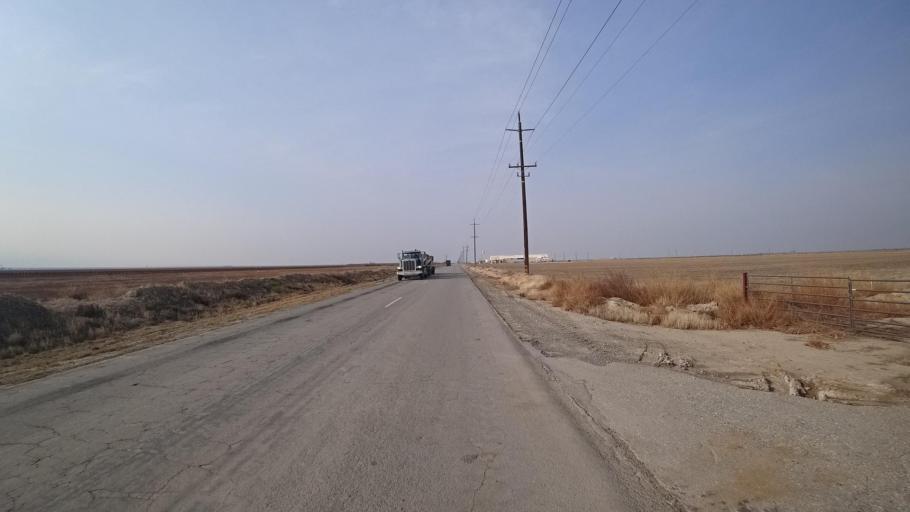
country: US
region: California
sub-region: Kern County
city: Greenfield
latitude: 35.0949
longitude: -119.0696
